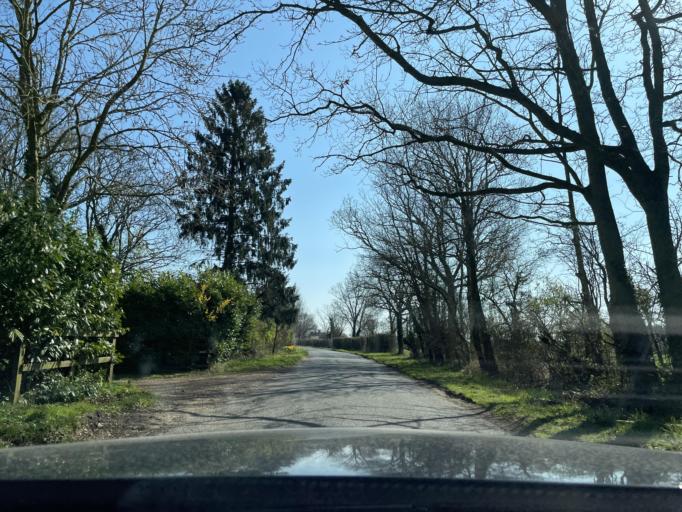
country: GB
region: England
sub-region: Norfolk
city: Hingham
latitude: 52.6198
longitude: 0.9825
